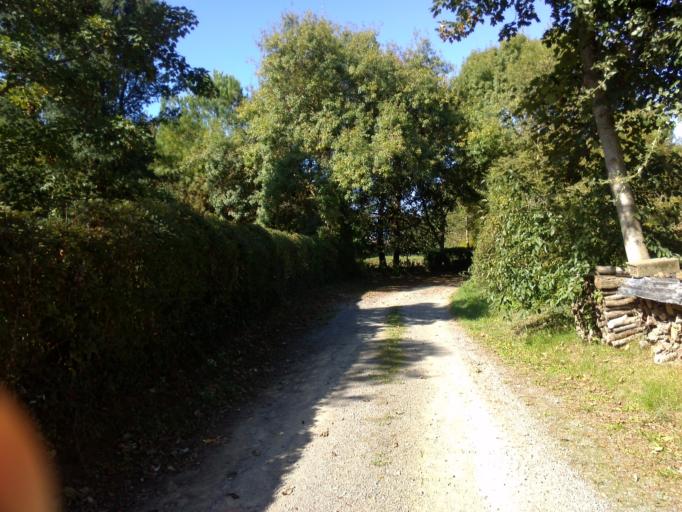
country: FR
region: Pays de la Loire
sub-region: Departement de la Loire-Atlantique
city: Chemere
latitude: 47.1219
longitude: -1.9224
